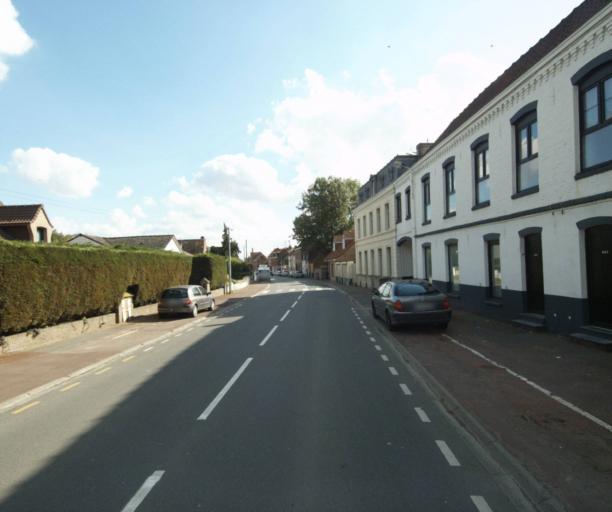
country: FR
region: Nord-Pas-de-Calais
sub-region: Departement du Nord
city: Sainghin-en-Weppes
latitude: 50.5683
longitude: 2.8924
